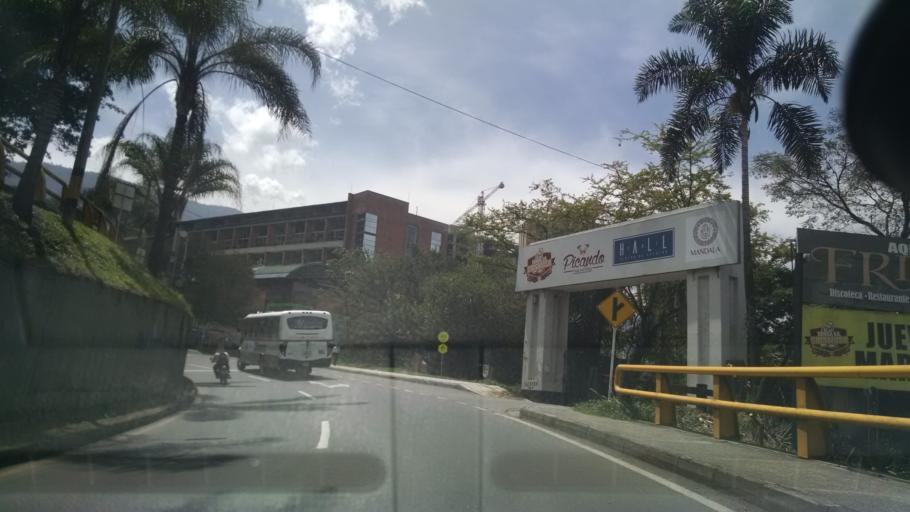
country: CO
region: Antioquia
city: Medellin
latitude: 6.2183
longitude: -75.5661
